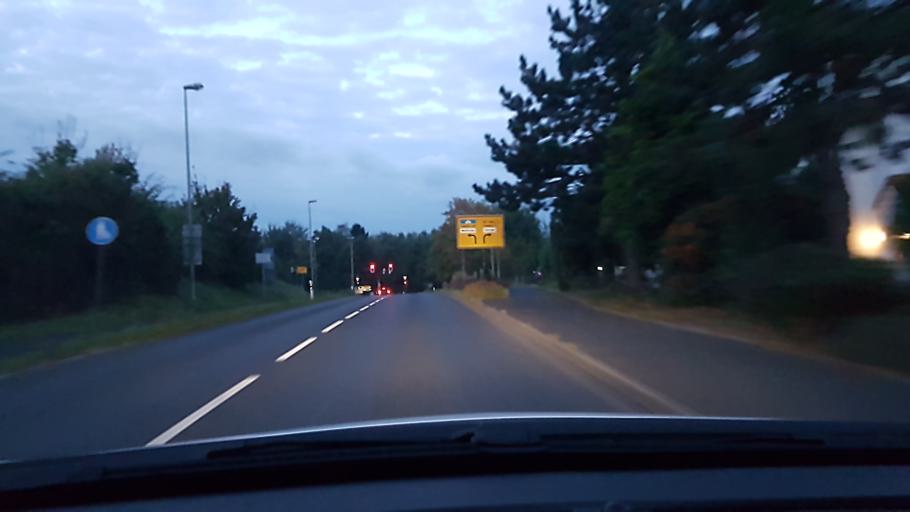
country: DE
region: Hesse
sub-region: Regierungsbezirk Darmstadt
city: Oberursel
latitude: 50.1936
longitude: 8.5713
